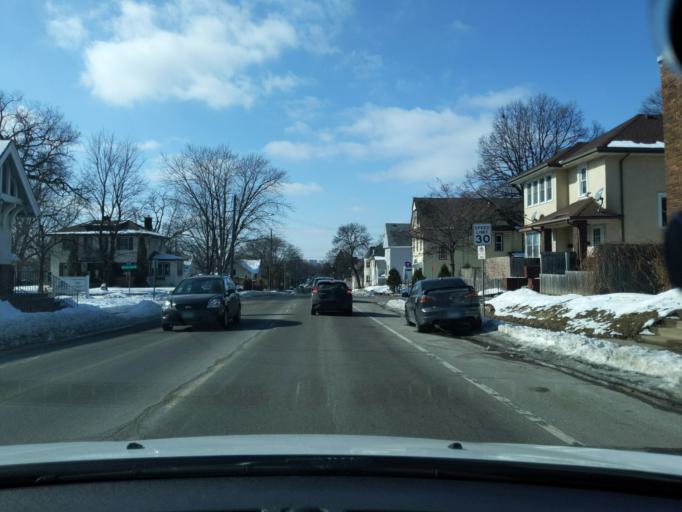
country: US
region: Minnesota
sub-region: Hennepin County
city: Saint Anthony
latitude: 45.0132
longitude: -93.2404
